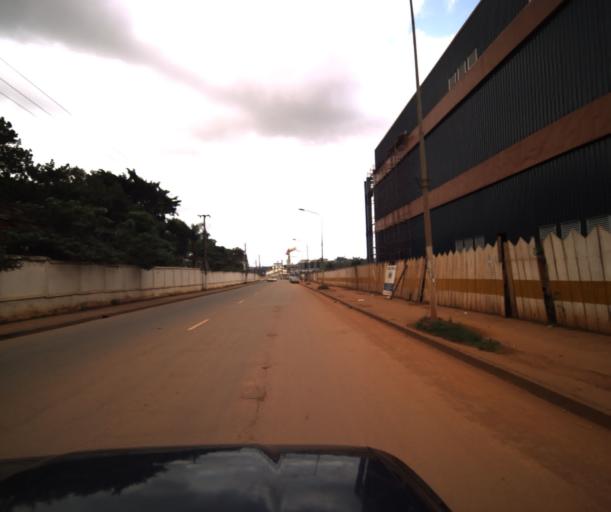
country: CM
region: Centre
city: Yaounde
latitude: 3.8437
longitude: 11.5162
